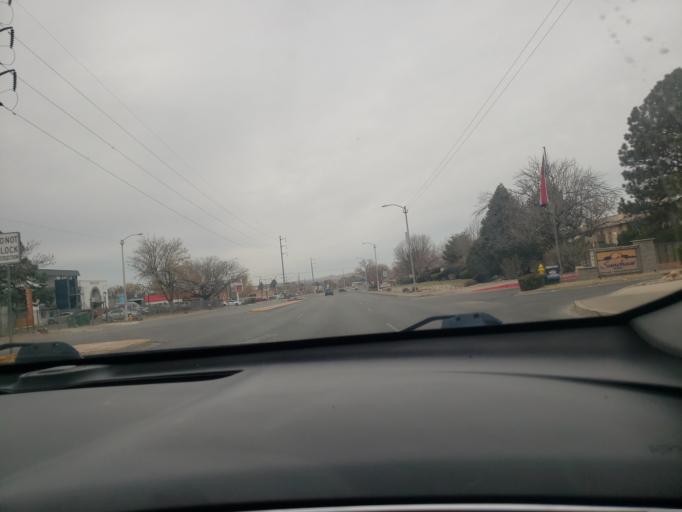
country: US
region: New Mexico
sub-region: Bernalillo County
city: North Valley
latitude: 35.1310
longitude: -106.6007
